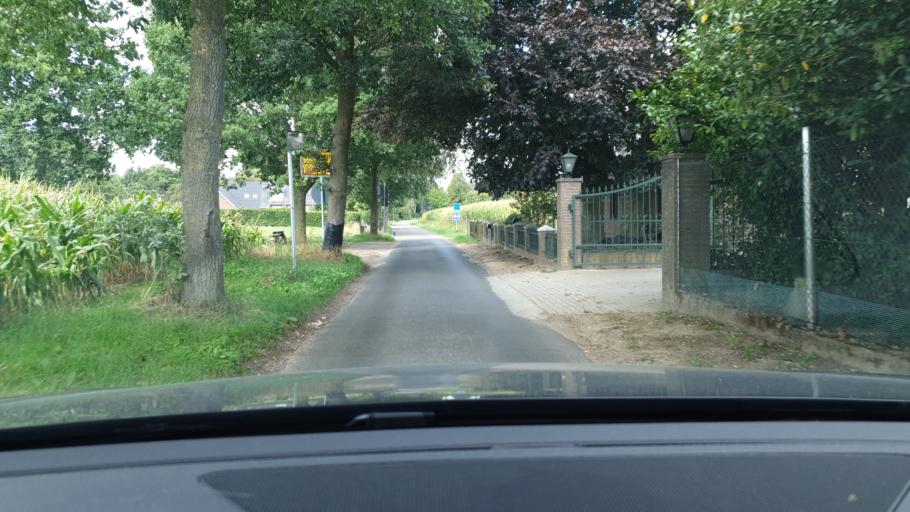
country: NL
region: Gelderland
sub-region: Gemeente Groesbeek
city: Bredeweg
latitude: 51.7506
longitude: 5.9557
